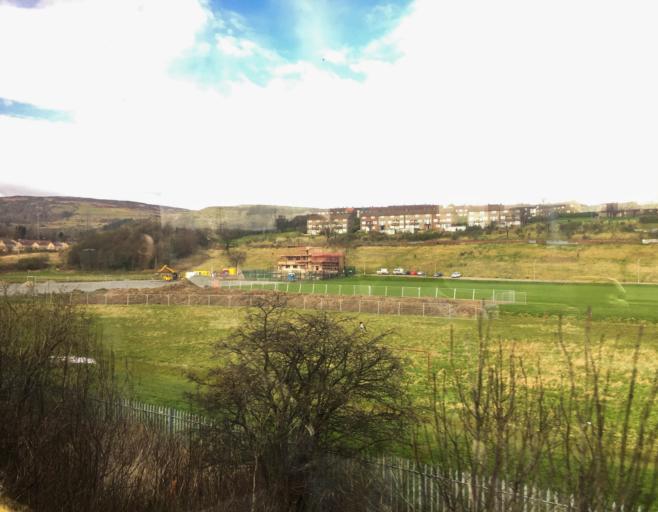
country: GB
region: Scotland
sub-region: West Dunbartonshire
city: Old Kilpatrick
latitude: 55.9164
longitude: -4.4375
